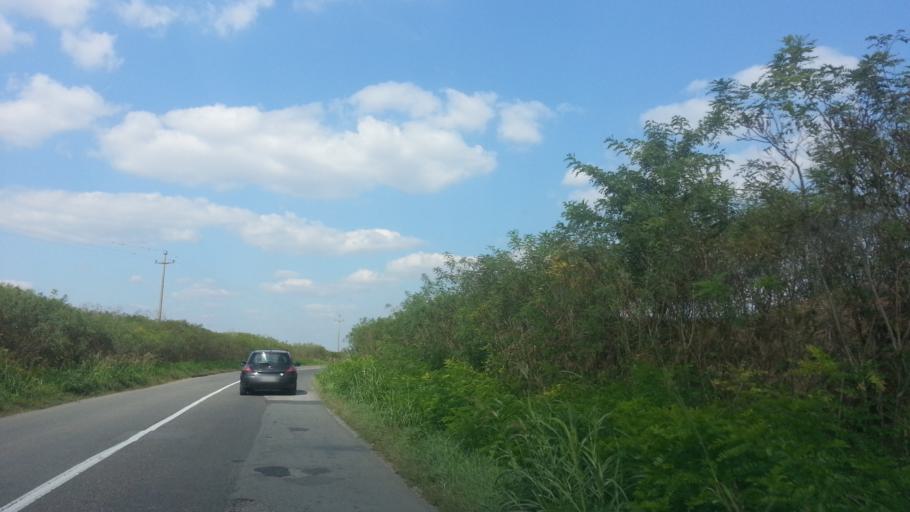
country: RS
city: Novi Banovci
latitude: 44.9274
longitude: 20.2798
